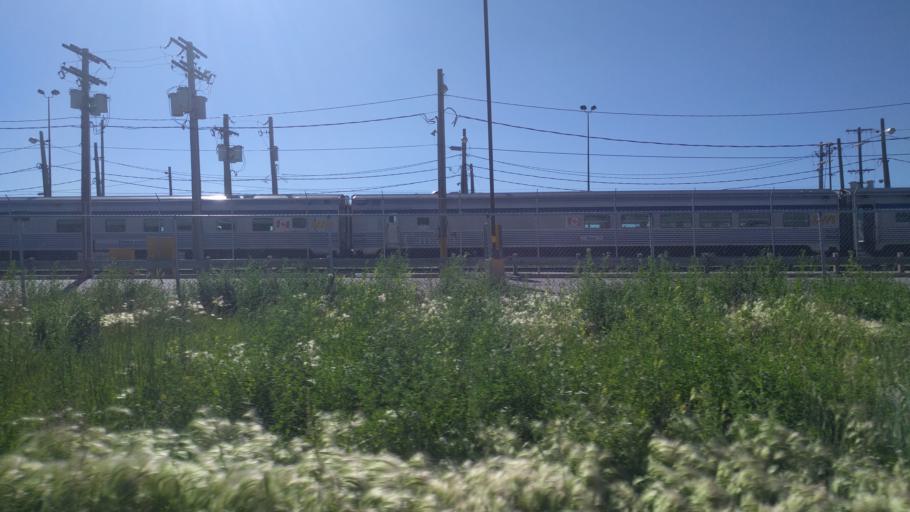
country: CA
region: Manitoba
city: Winnipeg
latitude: 49.8668
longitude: -97.1427
